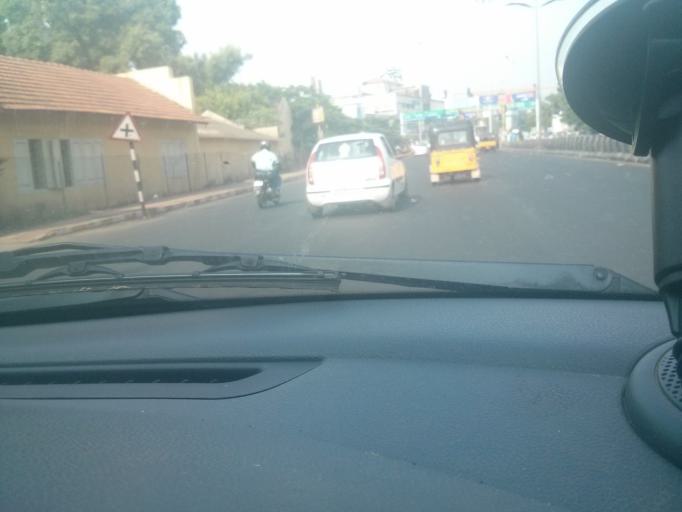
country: IN
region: Tamil Nadu
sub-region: Coimbatore
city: Coimbatore
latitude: 11.0135
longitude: 76.9867
